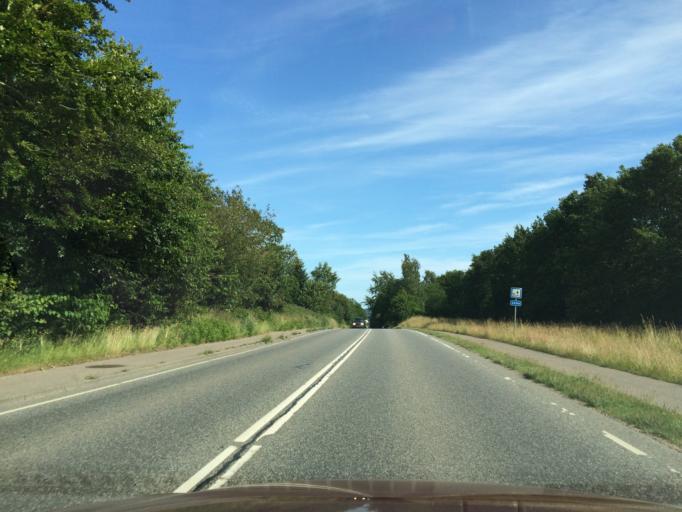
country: DK
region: Central Jutland
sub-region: Silkeborg Kommune
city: Silkeborg
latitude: 56.1917
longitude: 9.5327
